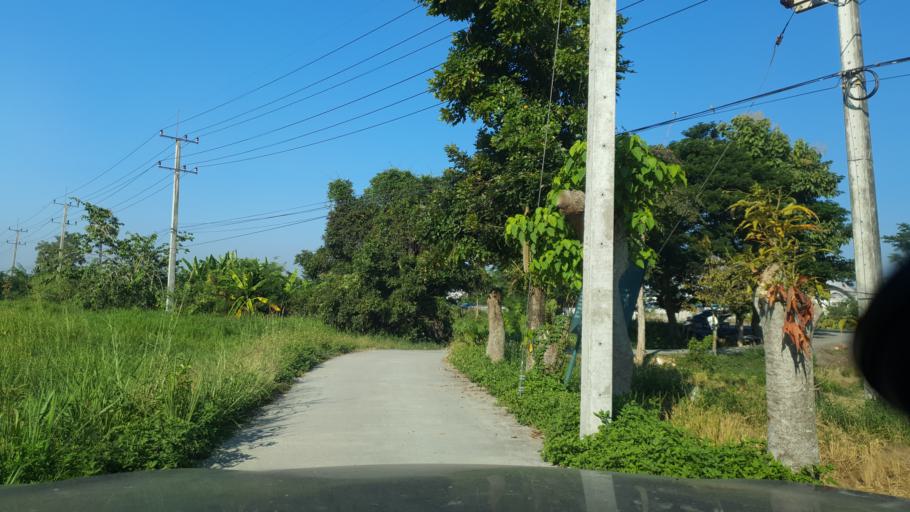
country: TH
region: Chiang Mai
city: San Kamphaeng
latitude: 18.7164
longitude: 99.1468
